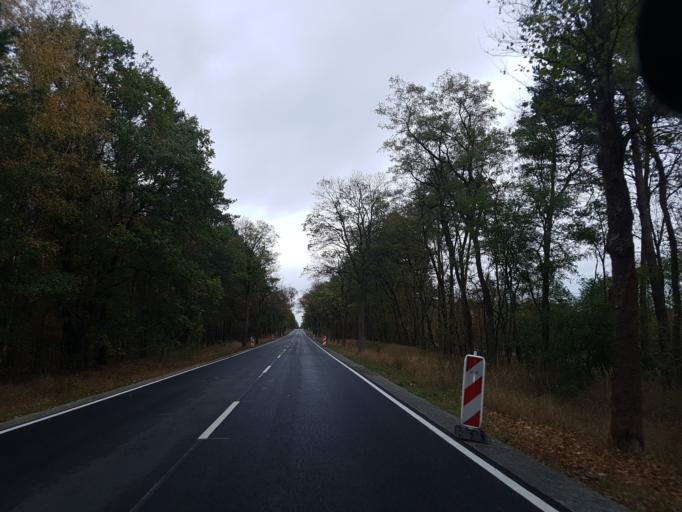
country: DE
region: Brandenburg
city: Treuenbrietzen
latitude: 52.0582
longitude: 12.8231
